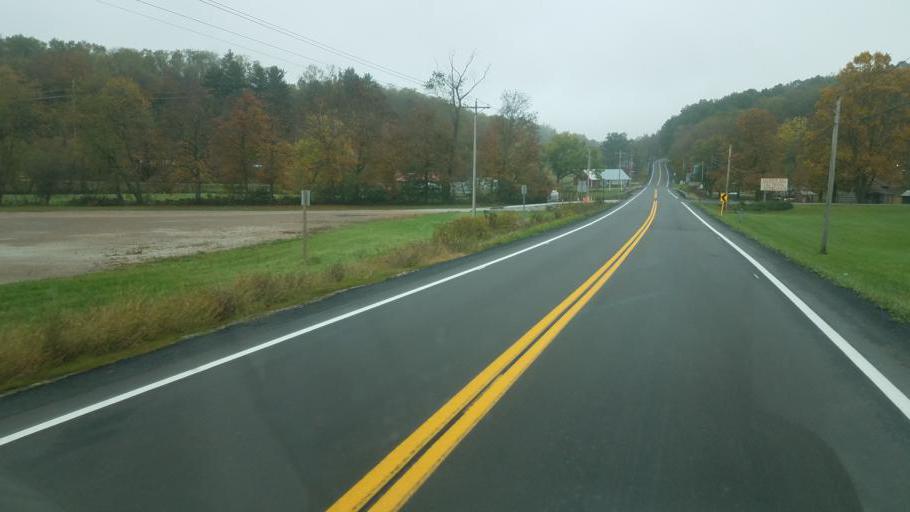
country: US
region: Ohio
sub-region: Carroll County
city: Carrollton
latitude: 40.5117
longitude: -81.1126
